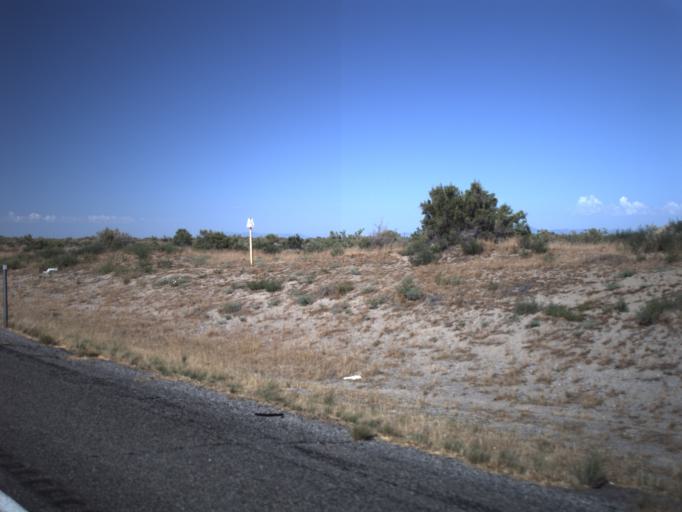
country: US
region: Utah
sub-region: Millard County
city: Delta
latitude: 39.4188
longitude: -112.4789
